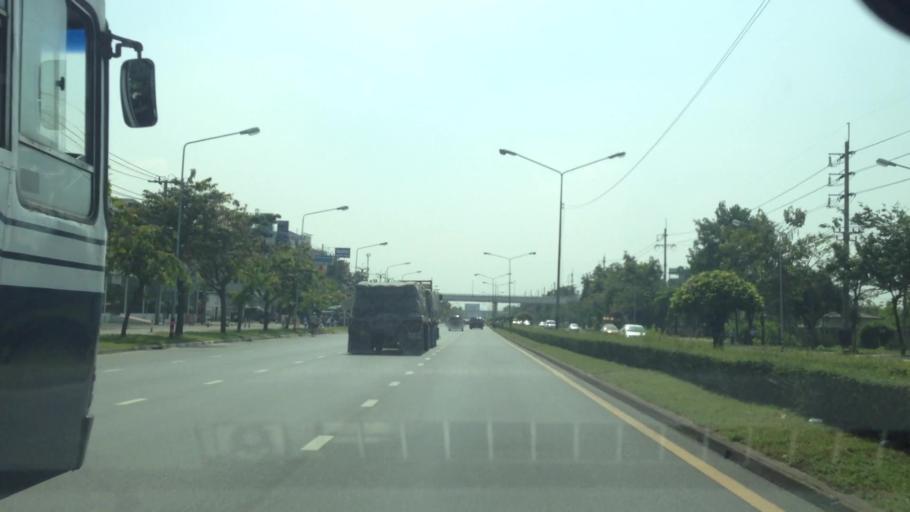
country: TH
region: Bangkok
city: Sai Mai
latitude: 13.9419
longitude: 100.6239
